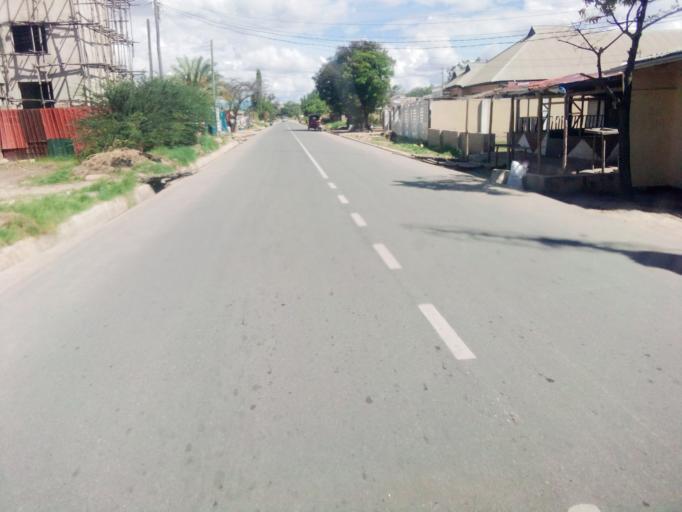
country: TZ
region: Dodoma
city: Dodoma
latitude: -6.1726
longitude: 35.7614
